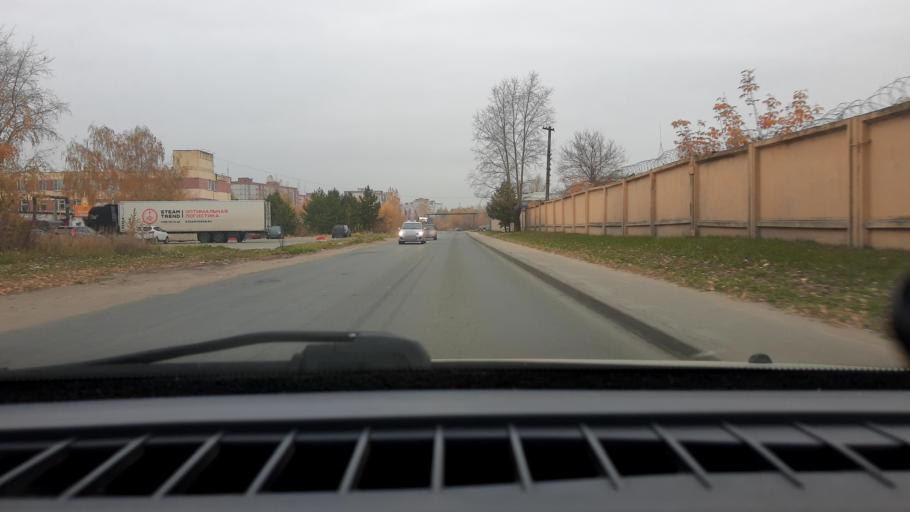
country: RU
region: Nizjnij Novgorod
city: Gorbatovka
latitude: 56.3373
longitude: 43.8065
